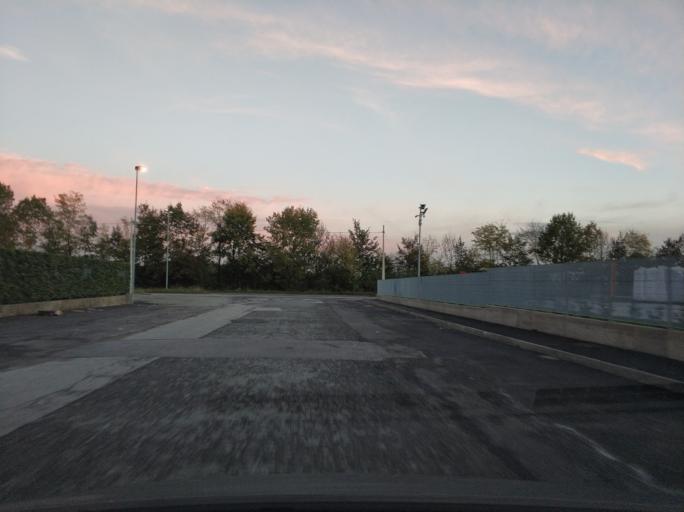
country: IT
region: Piedmont
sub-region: Provincia di Torino
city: Robassomero
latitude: 45.1763
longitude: 7.5988
